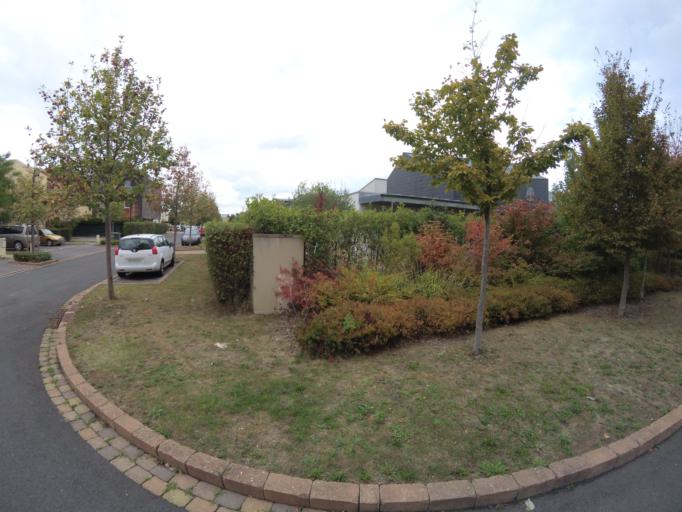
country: FR
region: Ile-de-France
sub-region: Departement de Seine-et-Marne
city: Chessy
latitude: 48.8793
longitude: 2.7734
